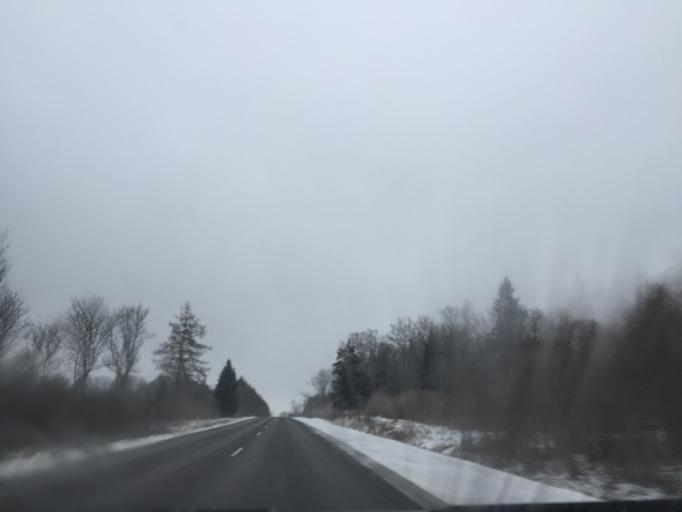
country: EE
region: Laeaene
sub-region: Lihula vald
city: Lihula
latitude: 58.5492
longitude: 23.9903
